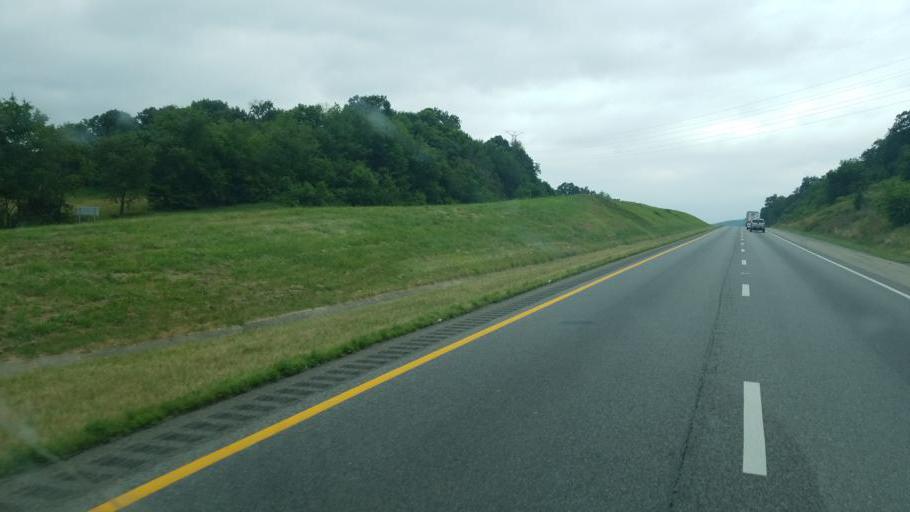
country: US
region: Virginia
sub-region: Wythe County
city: Wytheville
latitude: 36.9372
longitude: -80.9147
